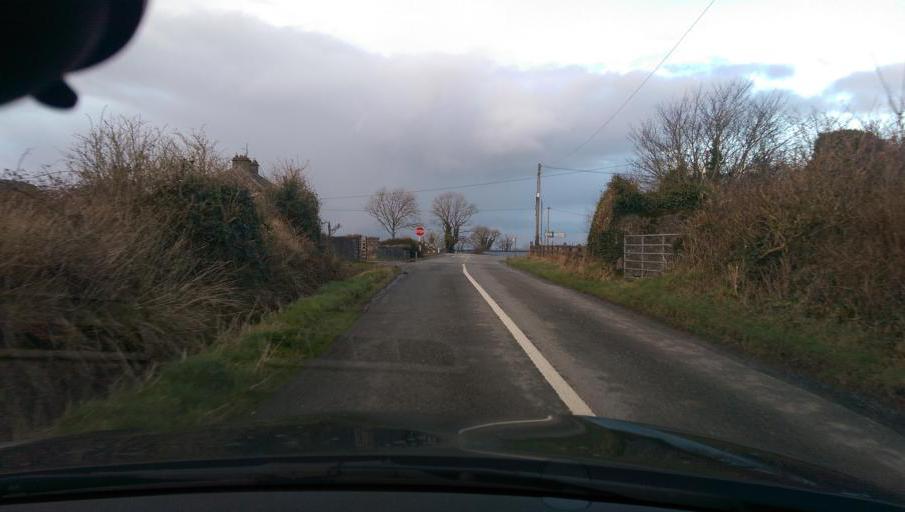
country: IE
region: Connaught
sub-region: County Galway
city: Ballinasloe
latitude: 53.4611
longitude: -8.3739
